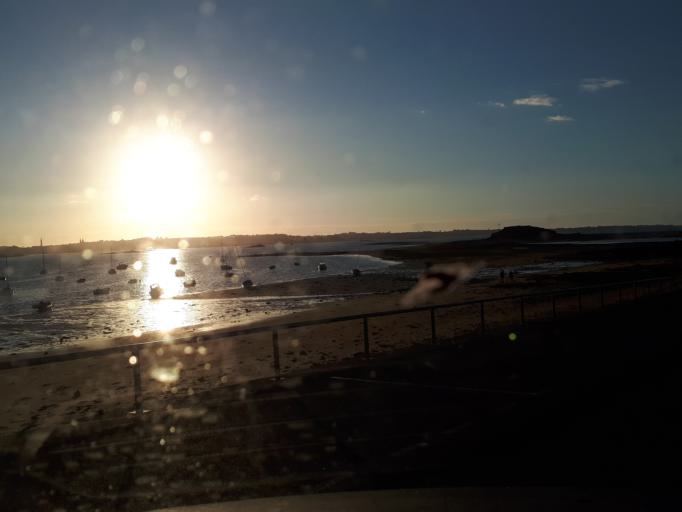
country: FR
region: Brittany
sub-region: Departement du Finistere
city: Carantec
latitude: 48.6732
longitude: -3.9231
